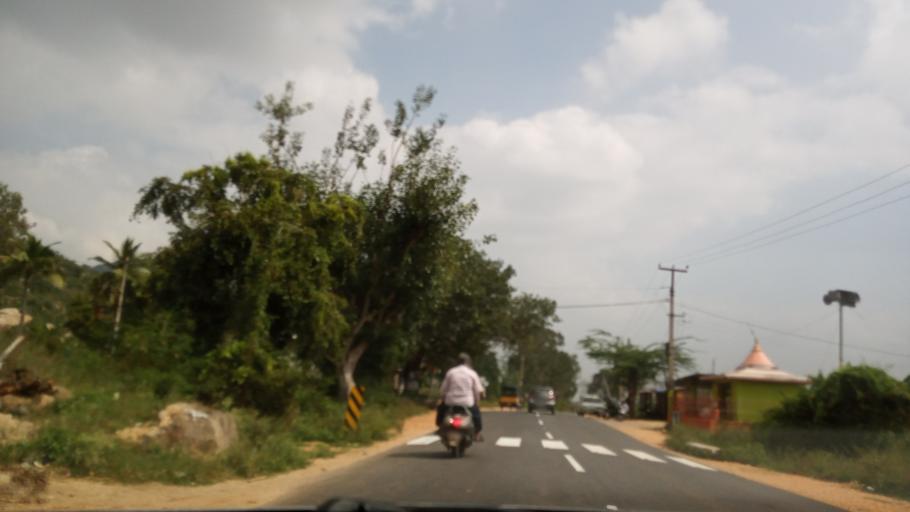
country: IN
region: Andhra Pradesh
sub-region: Chittoor
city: Madanapalle
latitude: 13.6364
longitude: 78.5966
